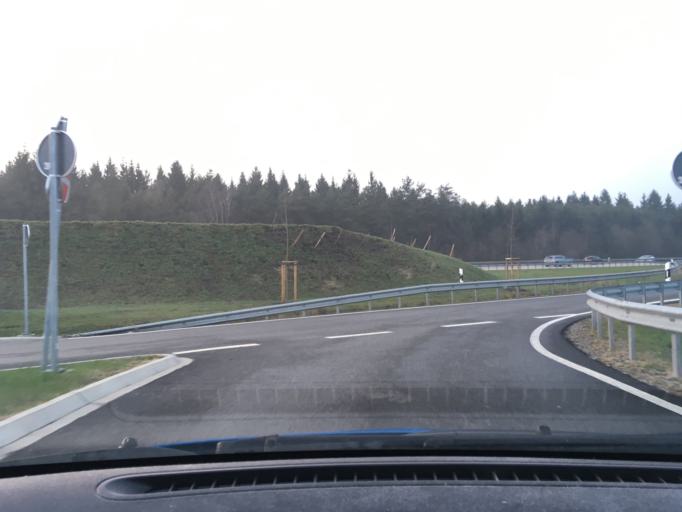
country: DE
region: Lower Saxony
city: Soltau
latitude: 52.9641
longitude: 9.9026
